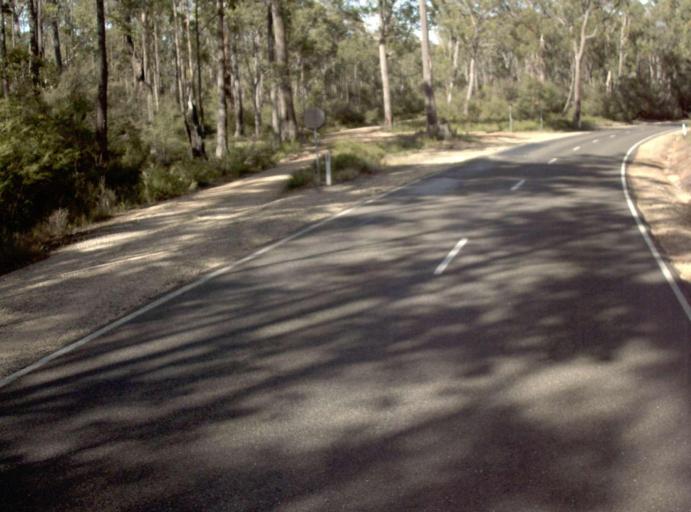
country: AU
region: Victoria
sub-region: East Gippsland
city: Lakes Entrance
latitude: -37.6653
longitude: 148.0763
